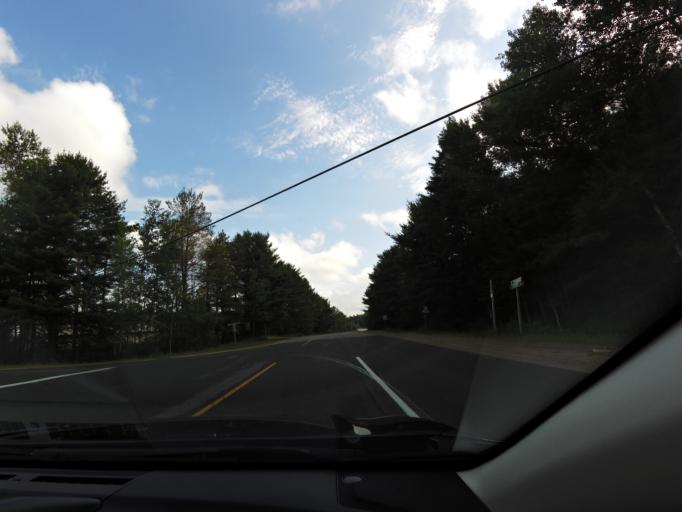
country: CA
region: Ontario
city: Bracebridge
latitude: 45.0330
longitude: -79.3026
